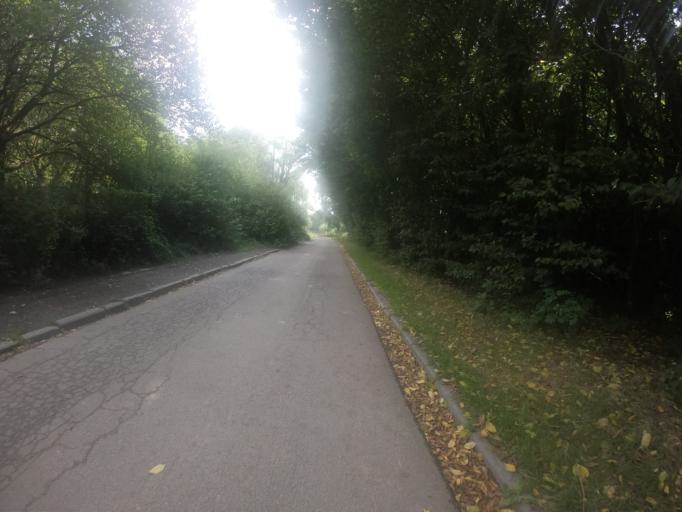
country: BE
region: Flanders
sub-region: Provincie Vlaams-Brabant
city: Dilbeek
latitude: 50.8285
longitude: 4.2739
